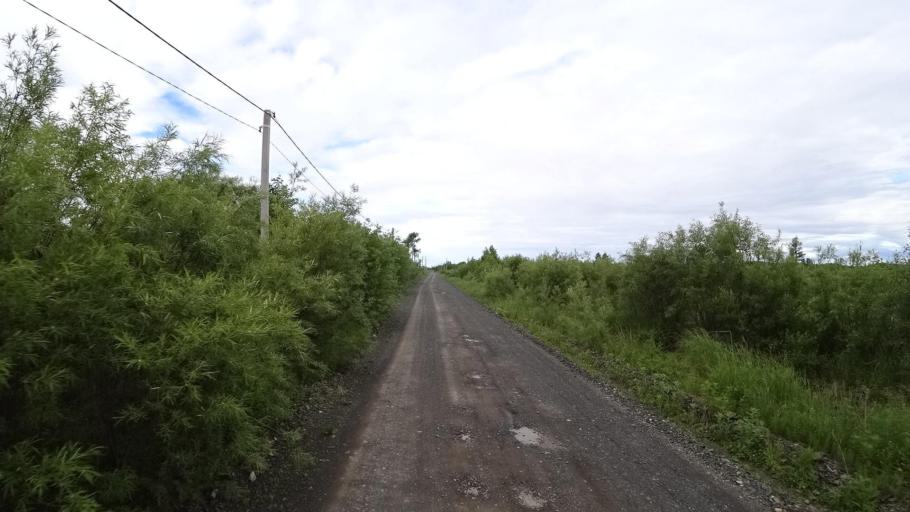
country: RU
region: Khabarovsk Krai
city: Amursk
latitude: 49.9081
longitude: 136.1486
